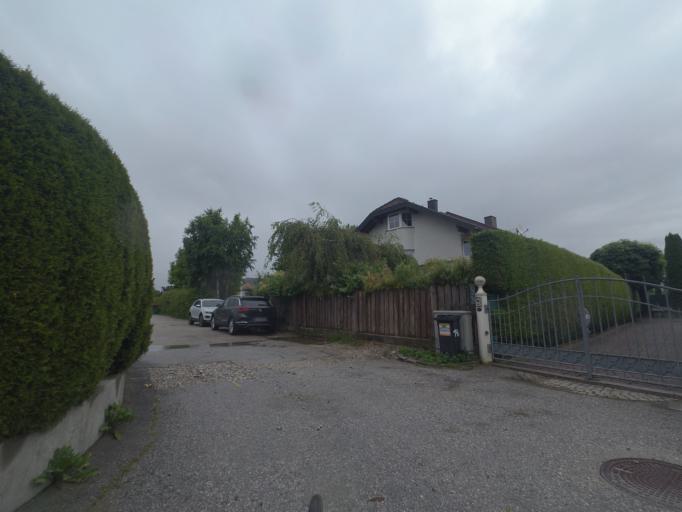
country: AT
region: Salzburg
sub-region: Politischer Bezirk Salzburg-Umgebung
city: Anif
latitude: 47.7462
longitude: 13.0521
